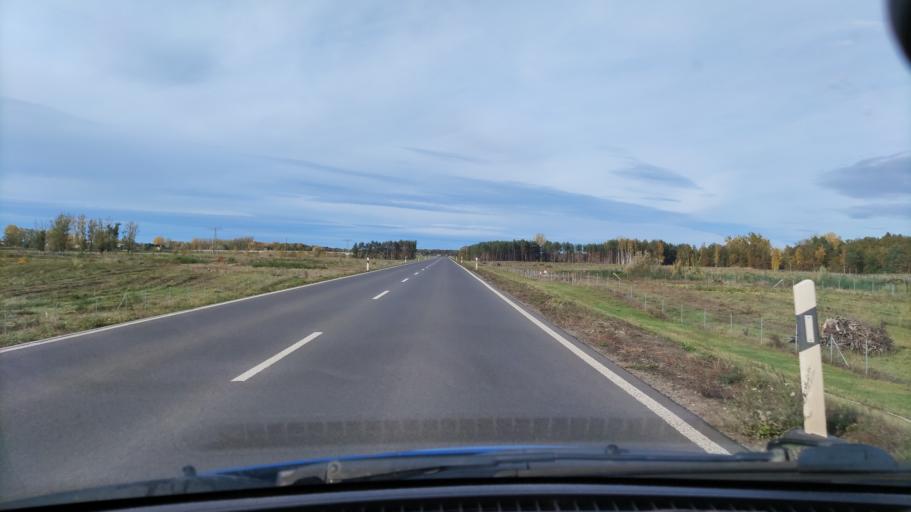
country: DE
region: Brandenburg
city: Breese
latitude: 53.0012
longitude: 11.7814
